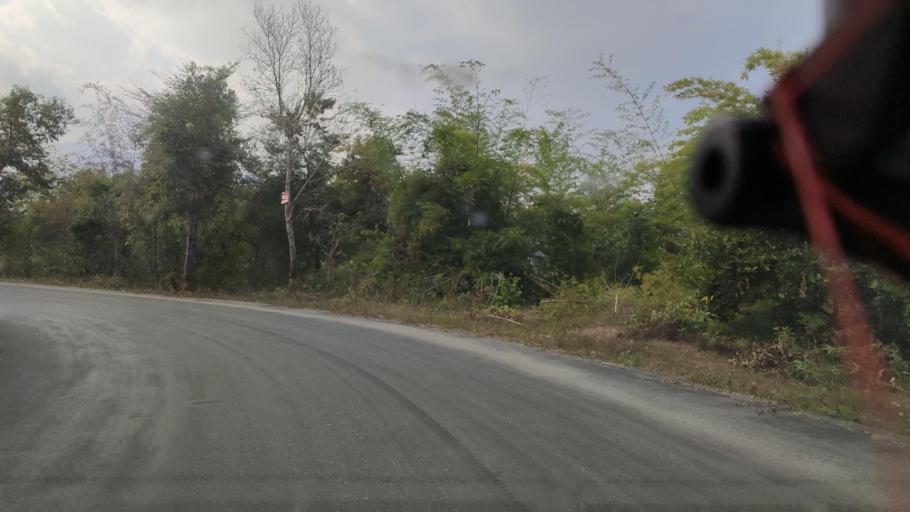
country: CN
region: Yunnan
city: Nayun
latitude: 21.4415
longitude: 99.6290
